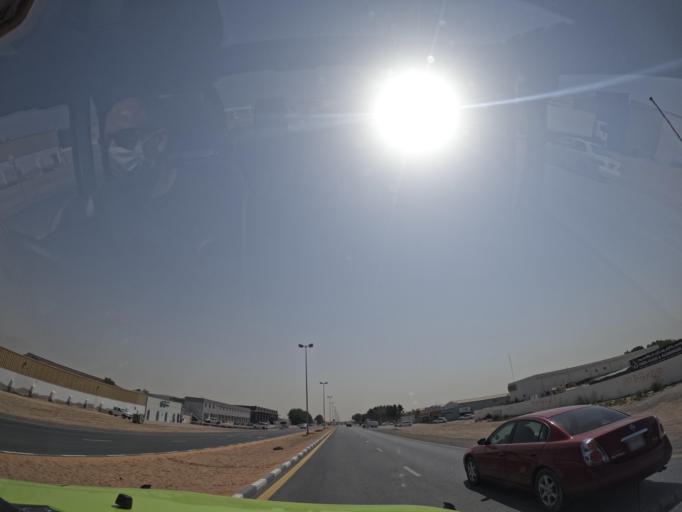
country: AE
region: Umm al Qaywayn
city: Umm al Qaywayn
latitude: 25.5042
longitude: 55.5608
